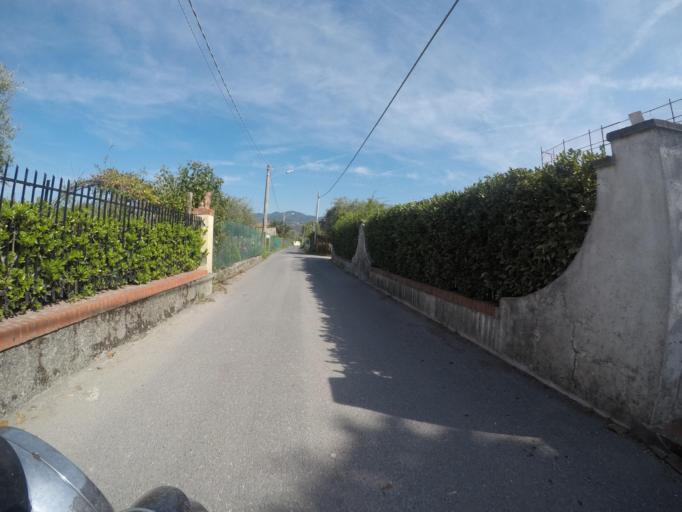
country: IT
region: Liguria
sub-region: Provincia di La Spezia
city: Casano-Dogana-Isola
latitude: 44.0573
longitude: 10.0323
